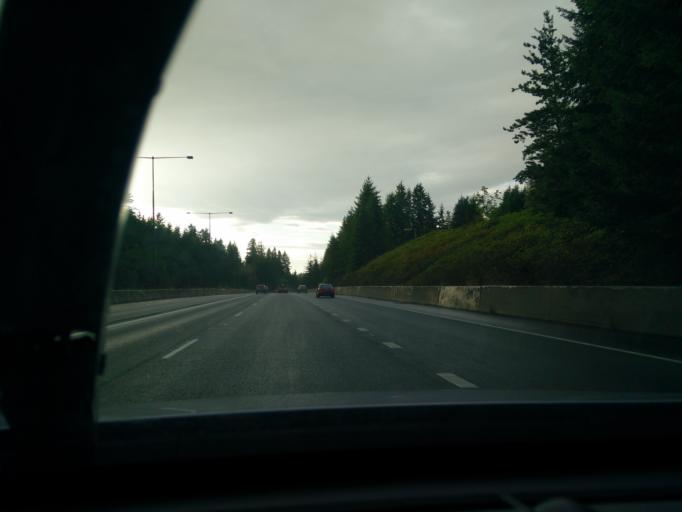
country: US
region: Washington
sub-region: Snohomish County
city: Martha Lake
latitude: 47.8223
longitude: -122.2469
